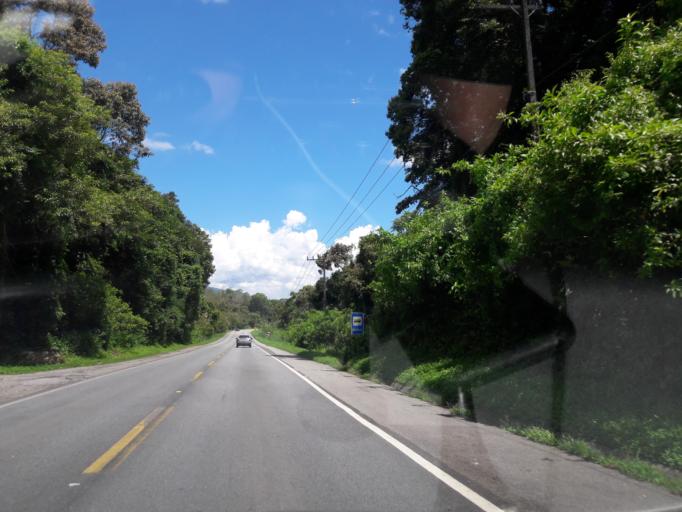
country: BR
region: Parana
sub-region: Antonina
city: Antonina
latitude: -25.4454
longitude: -48.7978
